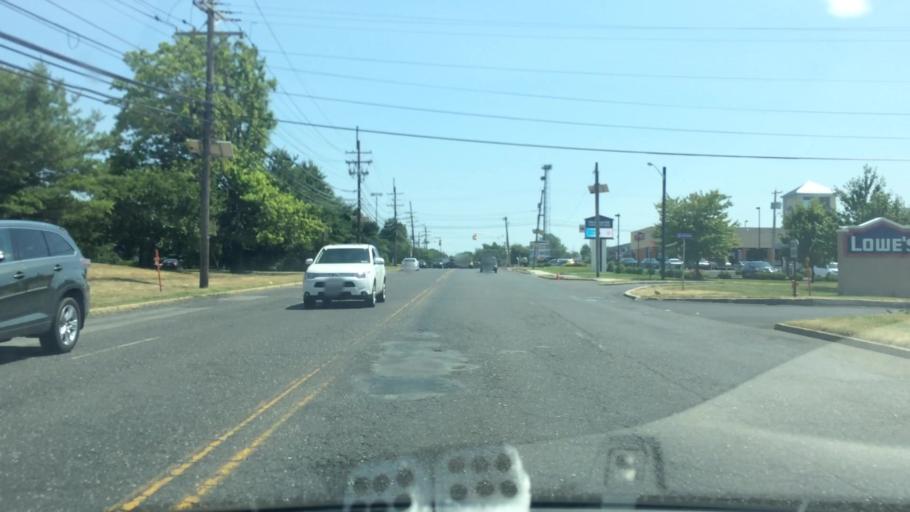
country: US
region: New Jersey
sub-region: Burlington County
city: Moorestown-Lenola
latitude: 39.9417
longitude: -74.9677
